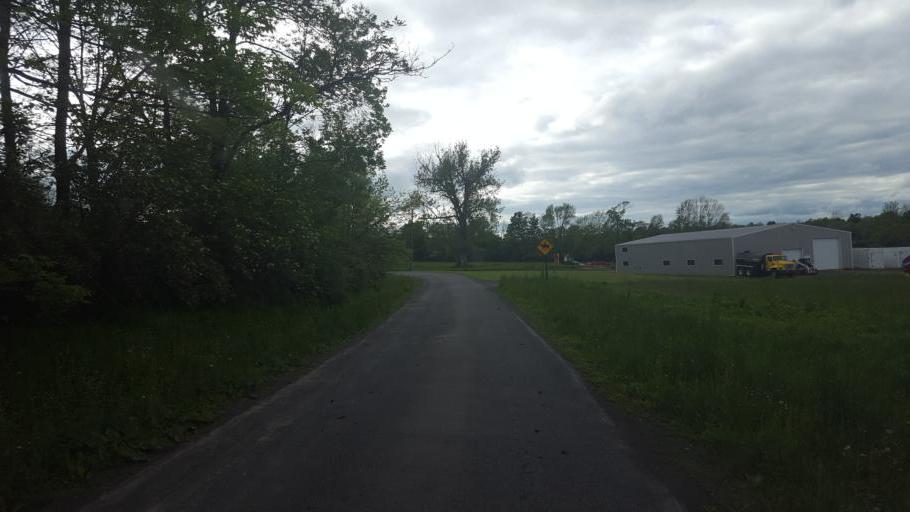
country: US
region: New York
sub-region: Otsego County
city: Richfield Springs
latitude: 42.8613
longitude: -74.9524
